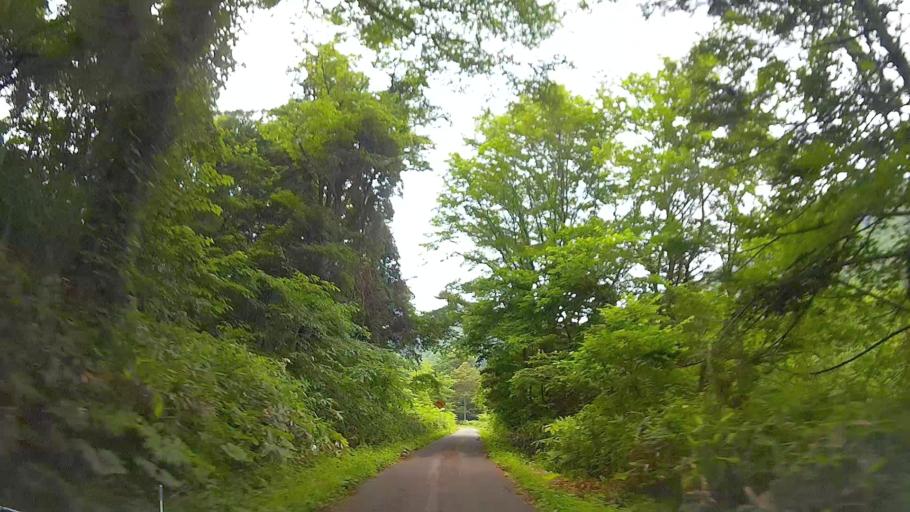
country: JP
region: Hokkaido
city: Nanae
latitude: 42.0488
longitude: 140.4917
